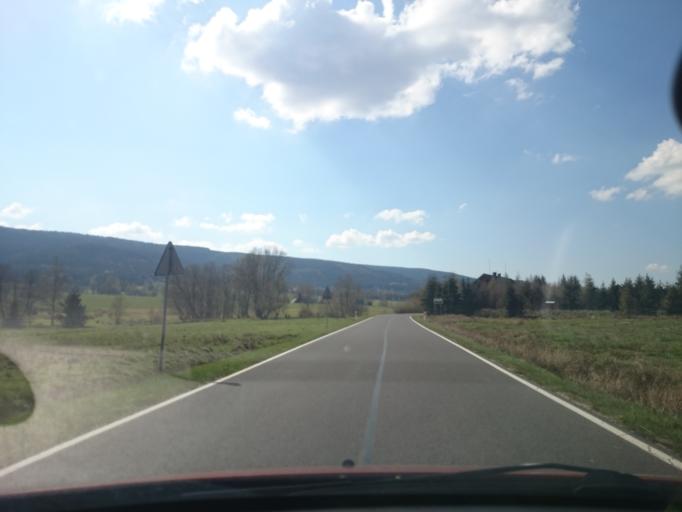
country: PL
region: Lower Silesian Voivodeship
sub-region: Powiat klodzki
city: Szczytna
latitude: 50.2973
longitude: 16.4628
